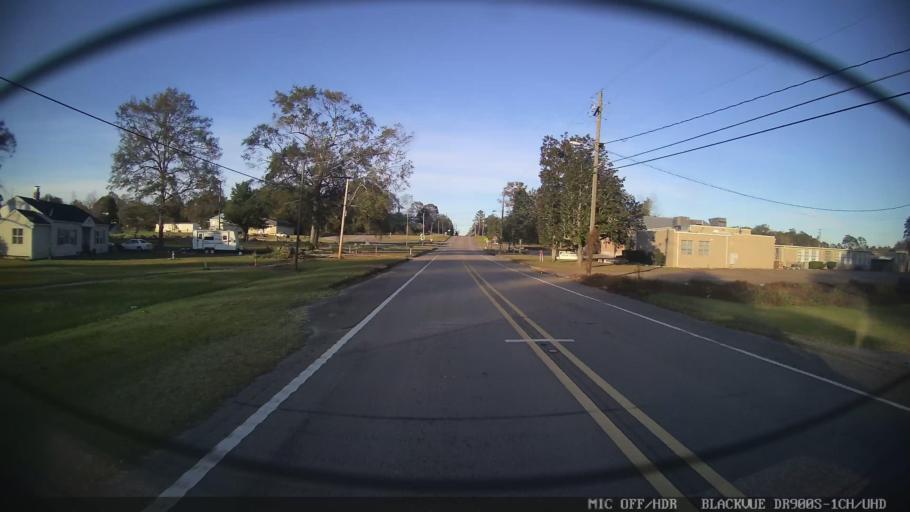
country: US
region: Mississippi
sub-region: Lamar County
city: Lumberton
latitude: 30.9972
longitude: -89.4544
